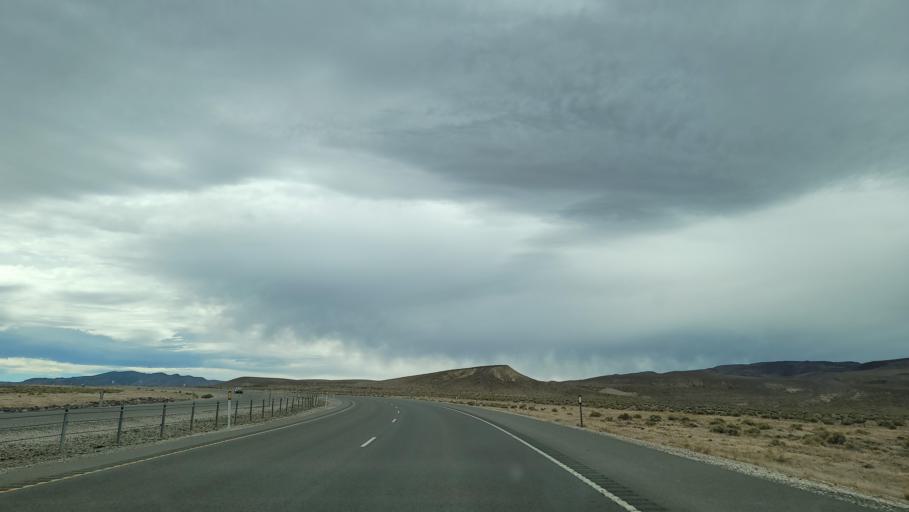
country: US
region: Nevada
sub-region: Lyon County
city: Silver Springs
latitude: 39.4071
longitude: -119.2710
